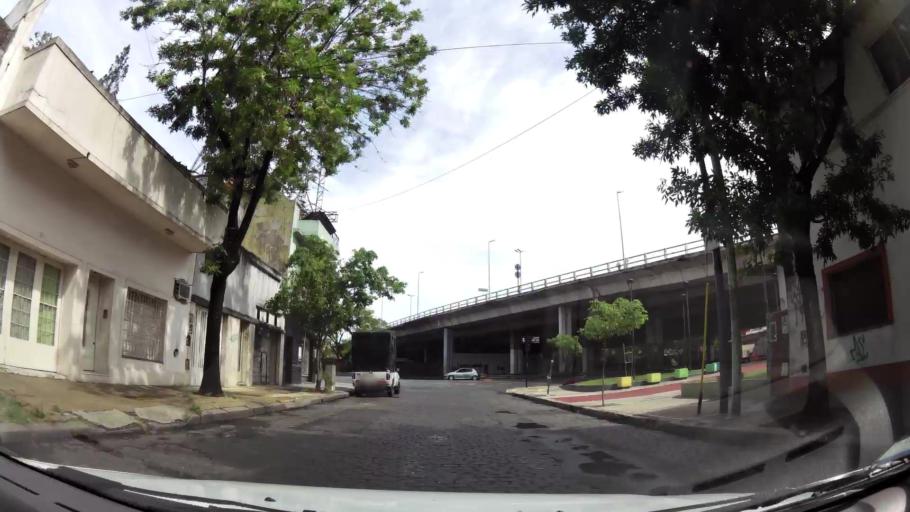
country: AR
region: Buenos Aires F.D.
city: Villa Santa Rita
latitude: -34.6365
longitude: -58.4951
